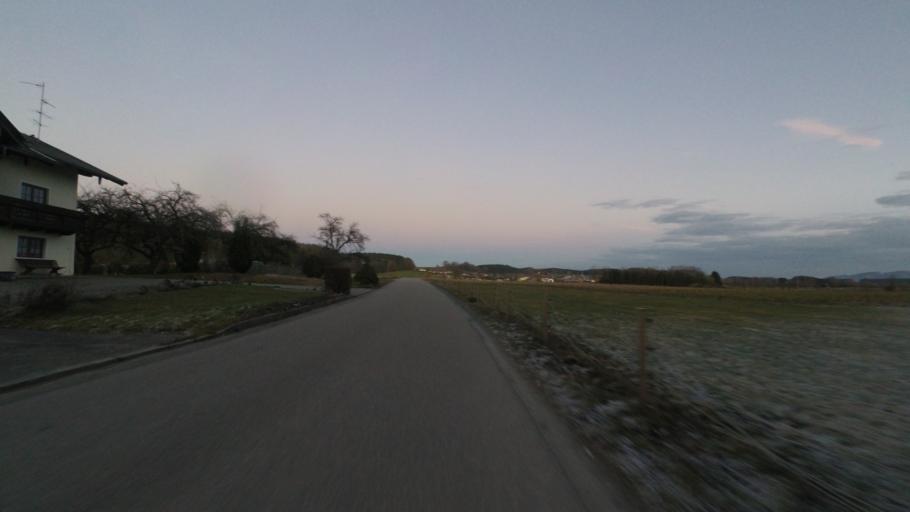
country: DE
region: Bavaria
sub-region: Upper Bavaria
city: Chieming
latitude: 47.9085
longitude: 12.5450
